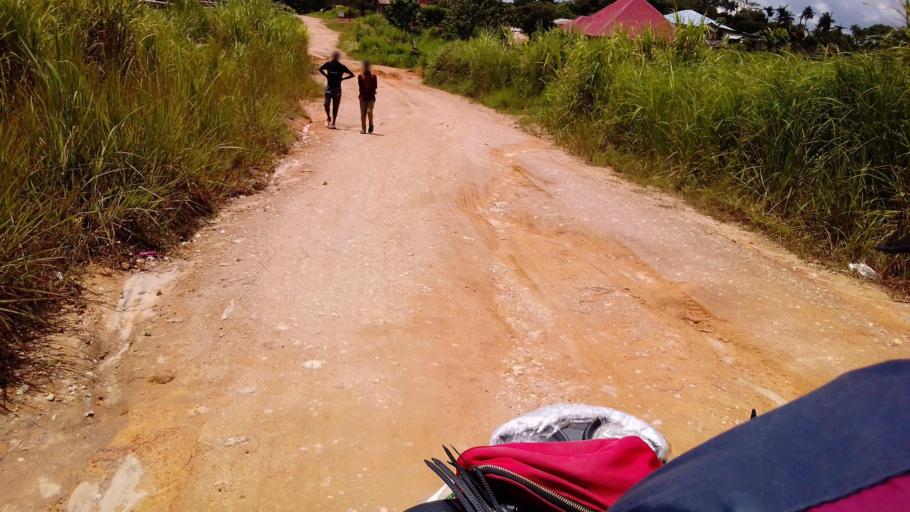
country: SL
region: Eastern Province
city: Koidu
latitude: 8.6663
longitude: -10.9727
